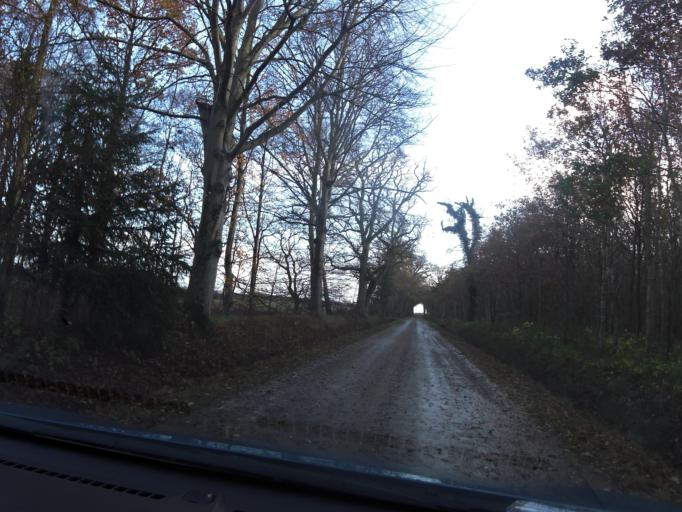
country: DK
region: Central Jutland
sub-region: Odder Kommune
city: Odder
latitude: 55.8553
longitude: 10.1634
